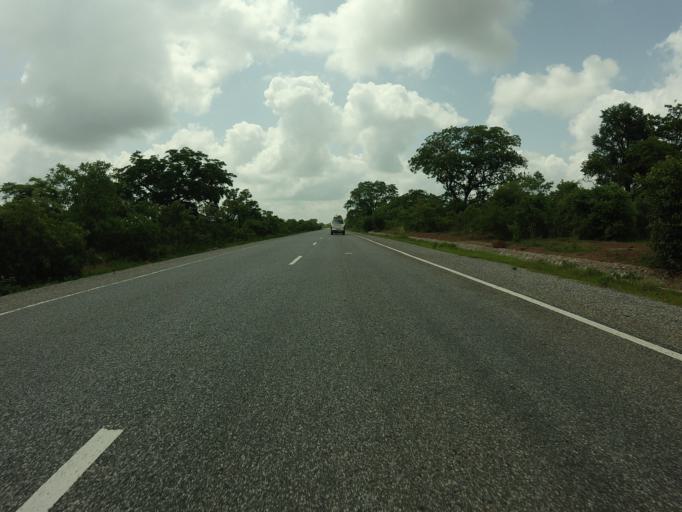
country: GH
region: Northern
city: Tamale
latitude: 9.1134
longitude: -1.6851
